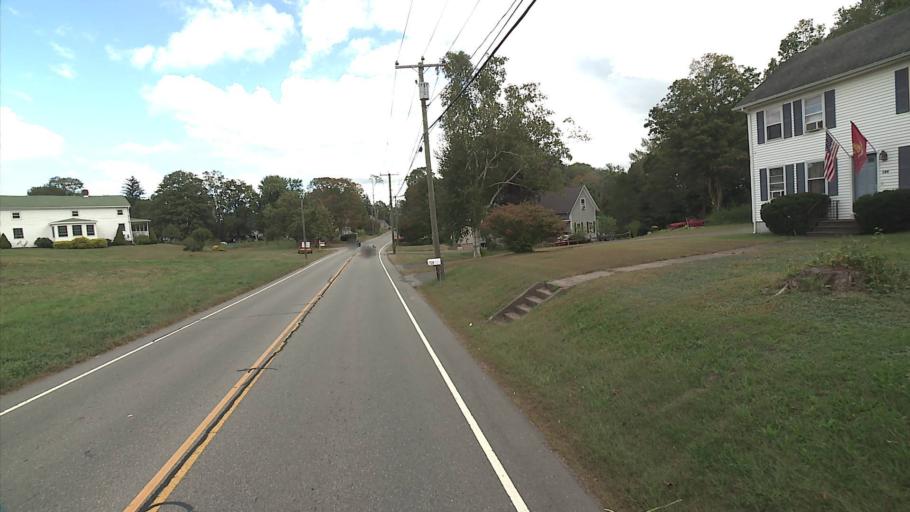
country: US
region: Connecticut
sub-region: Middlesex County
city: Durham
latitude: 41.5287
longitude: -72.6975
